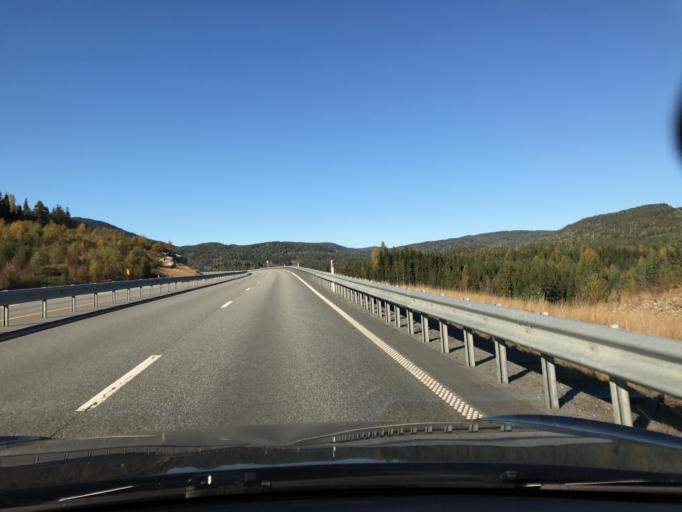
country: NO
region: Buskerud
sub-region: Krodsherad
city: Noresund
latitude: 60.2734
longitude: 9.7746
